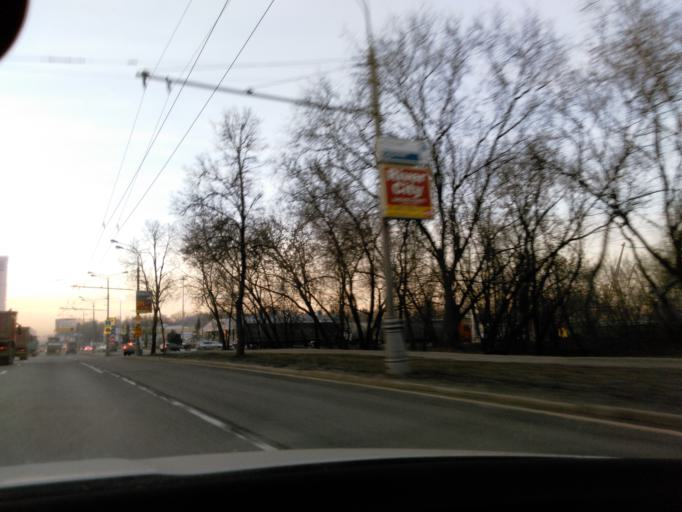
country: RU
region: Moskovskaya
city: Levoberezhnaya
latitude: 55.8668
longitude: 37.4621
